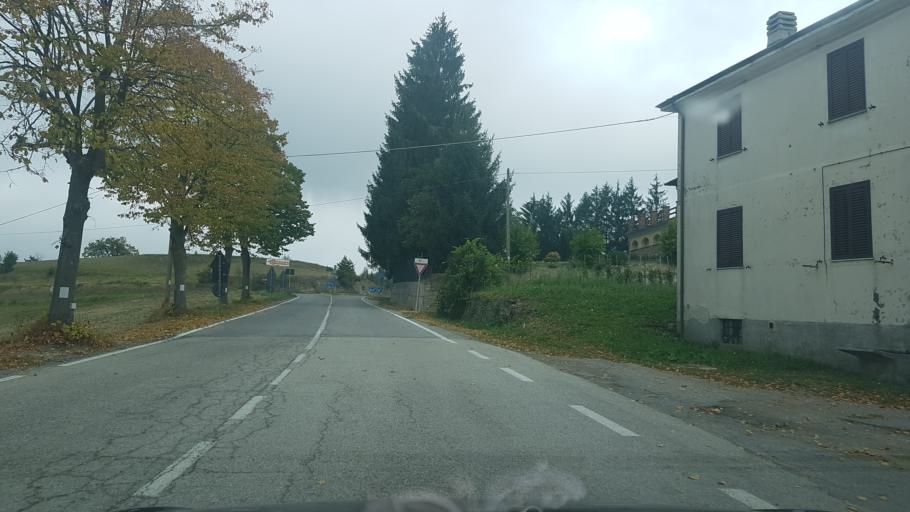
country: IT
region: Piedmont
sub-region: Provincia di Cuneo
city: Paroldo
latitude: 44.4242
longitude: 8.0955
